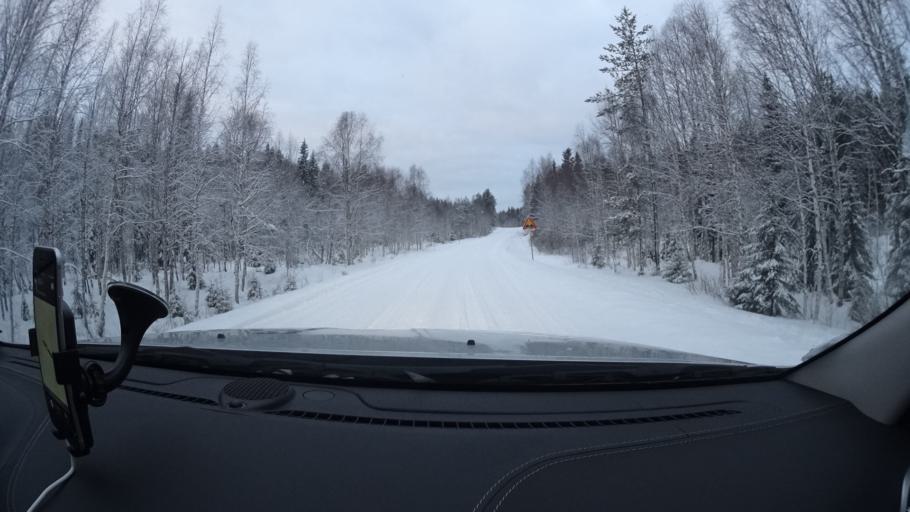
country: FI
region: Lapland
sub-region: Rovaniemi
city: Ranua
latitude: 66.3644
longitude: 26.6826
